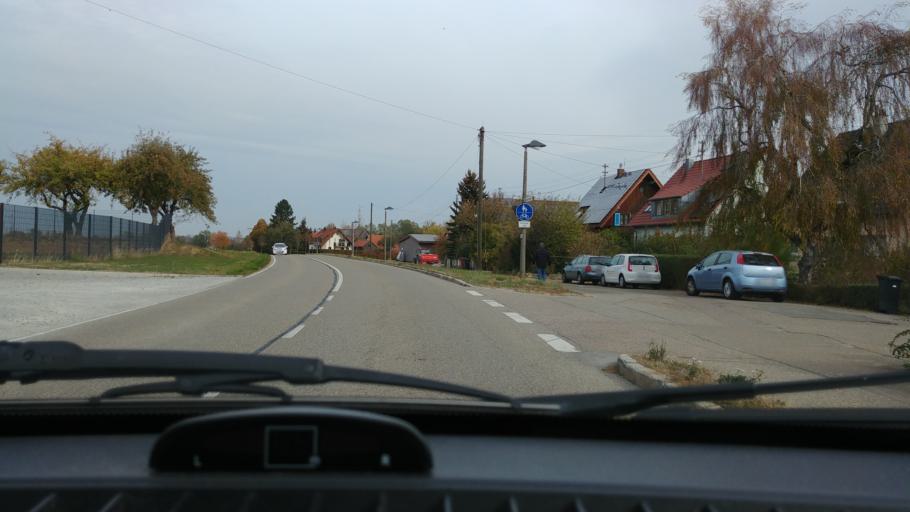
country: DE
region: Baden-Wuerttemberg
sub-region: Regierungsbezirk Stuttgart
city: Crailsheim
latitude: 49.0971
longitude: 10.0655
